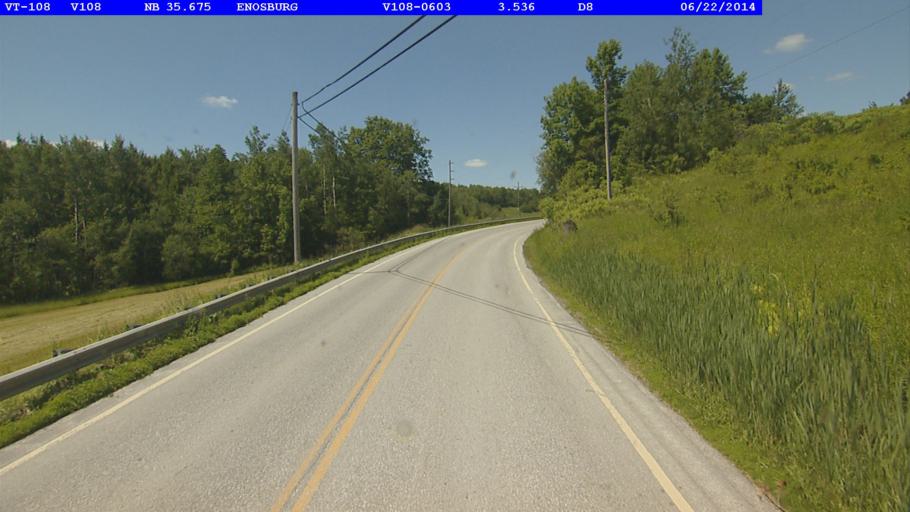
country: US
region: Vermont
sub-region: Franklin County
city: Enosburg Falls
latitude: 44.8867
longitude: -72.8024
